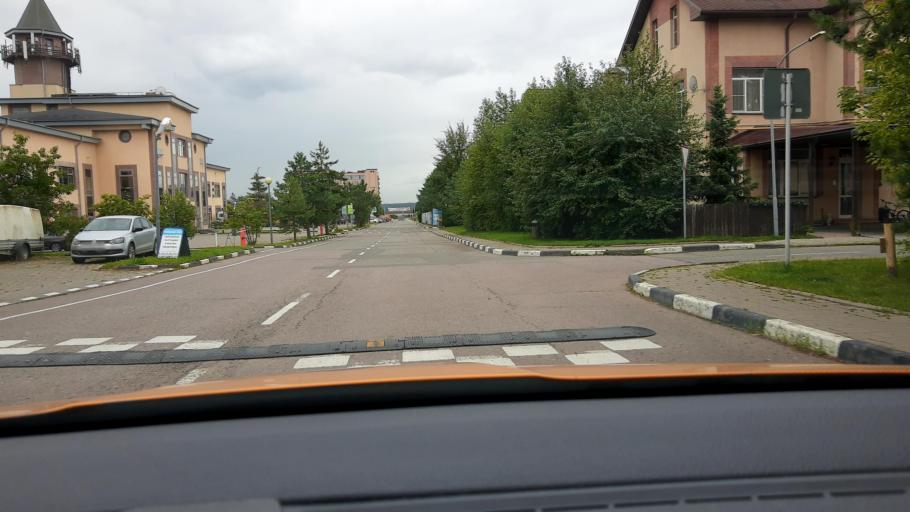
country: RU
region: Moskovskaya
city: Kommunarka
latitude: 55.5719
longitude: 37.4513
